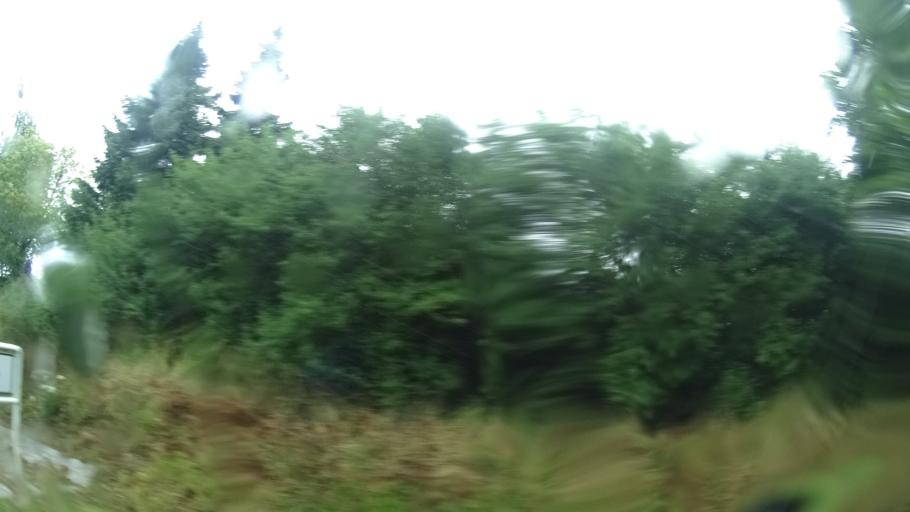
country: LU
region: Grevenmacher
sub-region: Canton de Remich
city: Mondorf-les-Bains
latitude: 49.5146
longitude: 6.3078
